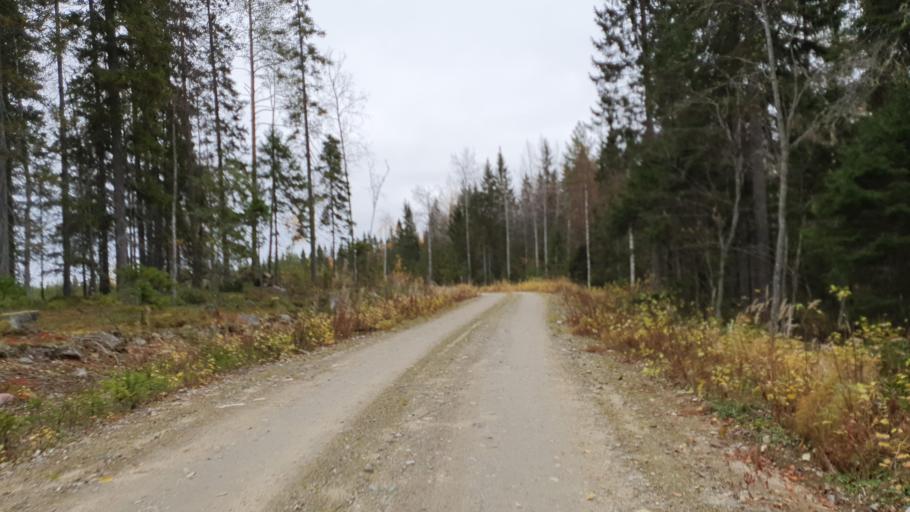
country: FI
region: Kainuu
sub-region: Kehys-Kainuu
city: Kuhmo
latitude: 64.4446
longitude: 29.6429
